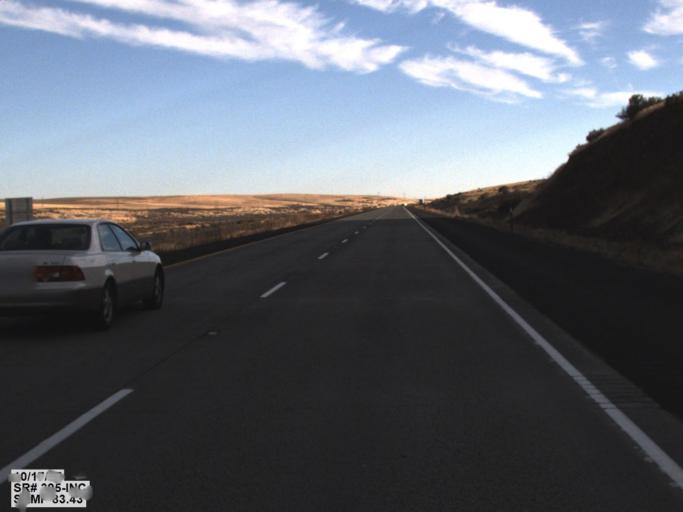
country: US
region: Washington
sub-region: Adams County
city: Ritzville
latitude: 46.9867
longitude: -118.5574
